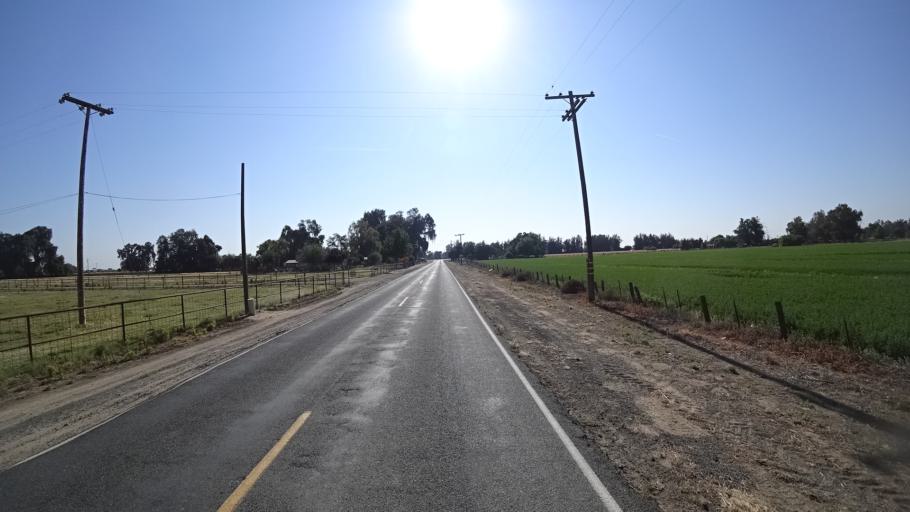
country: US
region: California
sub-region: Kings County
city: Lemoore
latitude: 36.3658
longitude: -119.8136
